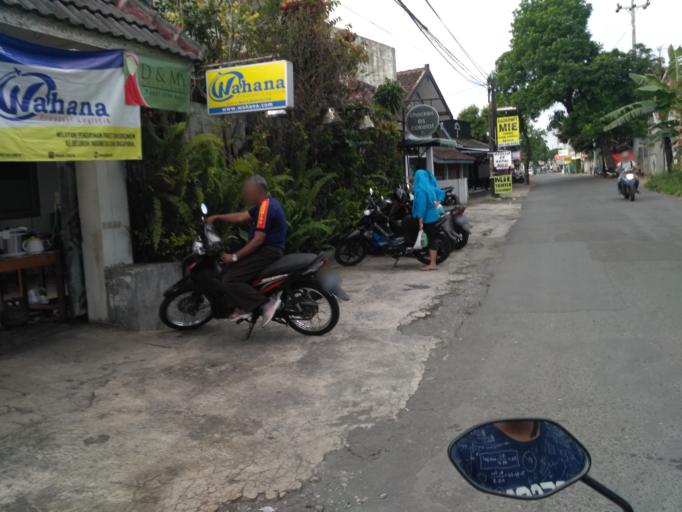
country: ID
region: Daerah Istimewa Yogyakarta
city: Melati
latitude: -7.7562
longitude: 110.3749
